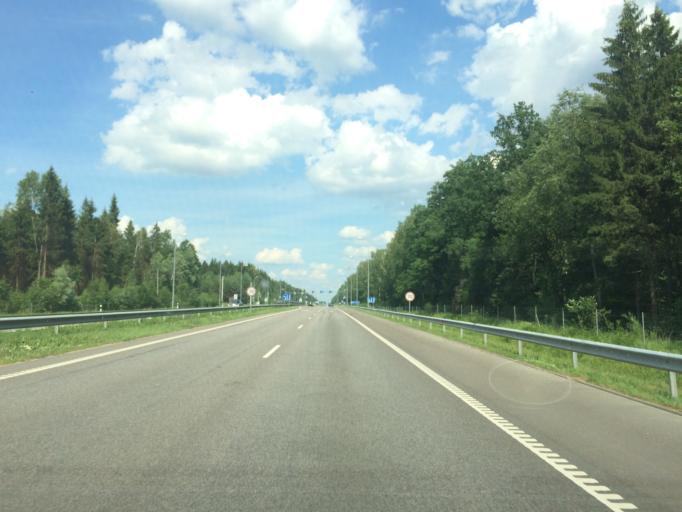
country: LT
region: Kauno apskritis
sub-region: Kauno rajonas
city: Karmelava
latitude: 55.0099
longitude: 24.1545
